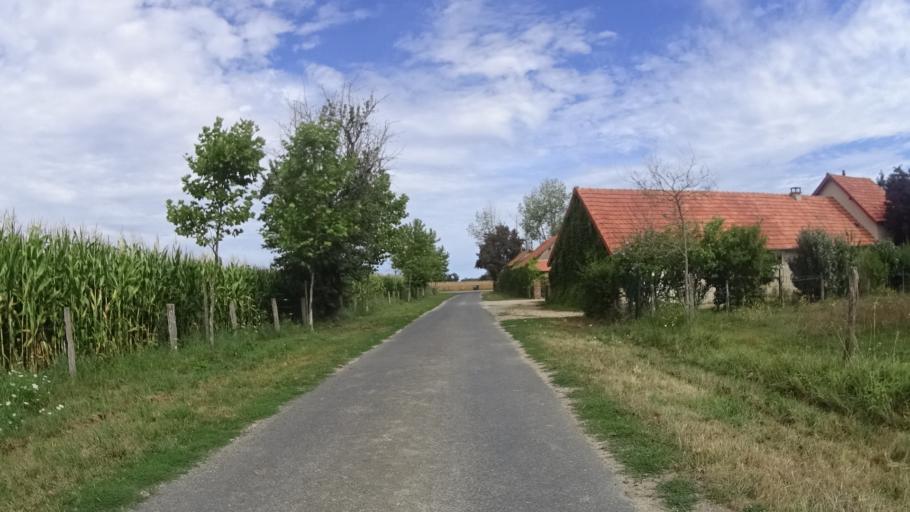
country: FR
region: Auvergne
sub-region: Departement de l'Allier
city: Beaulon
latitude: 46.6522
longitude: 3.6663
